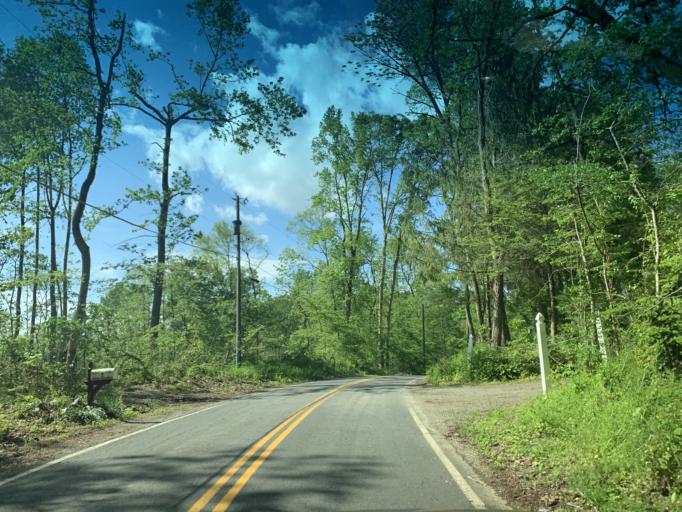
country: US
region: Maryland
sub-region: Cecil County
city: Rising Sun
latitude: 39.6916
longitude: -76.1867
